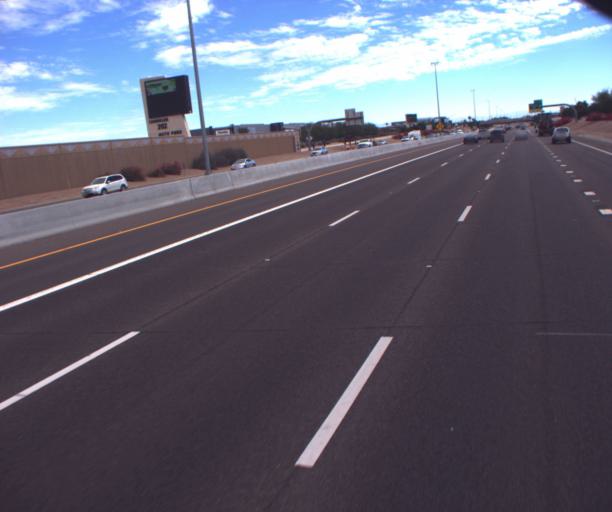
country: US
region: Arizona
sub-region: Maricopa County
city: Chandler
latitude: 33.2827
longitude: -111.7980
